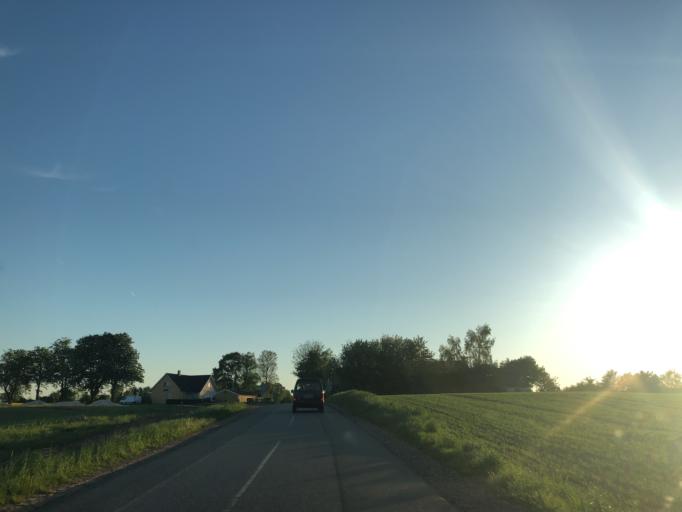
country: DK
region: Zealand
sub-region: Ringsted Kommune
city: Ringsted
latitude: 55.4068
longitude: 11.8624
